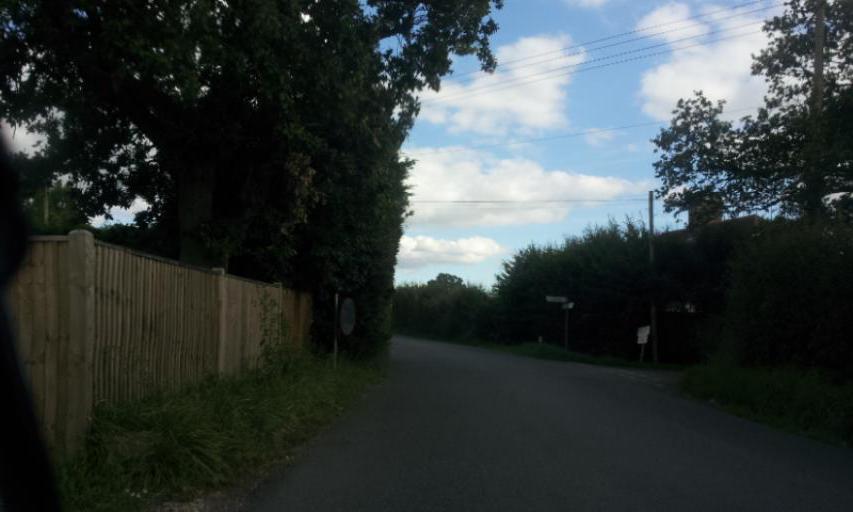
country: GB
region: England
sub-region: Kent
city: Headcorn
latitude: 51.1751
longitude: 0.5992
